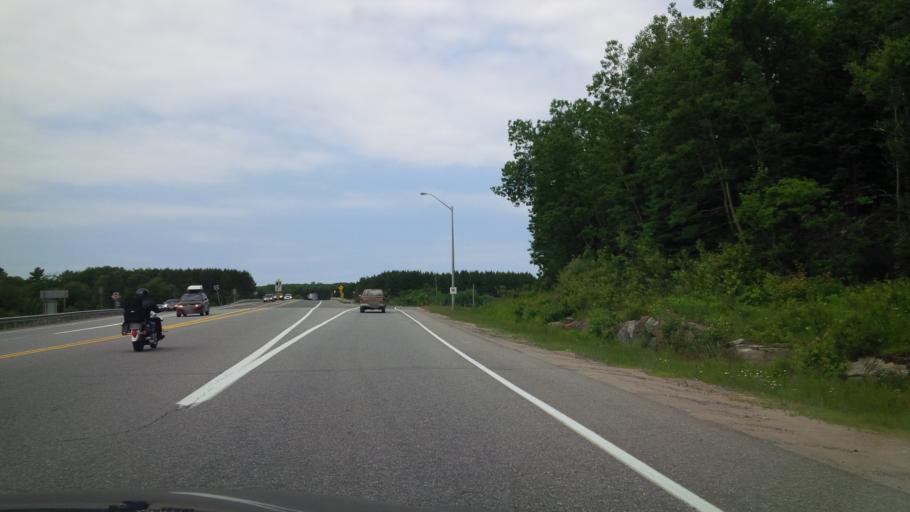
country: CA
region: Ontario
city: Huntsville
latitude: 45.3459
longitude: -79.2276
